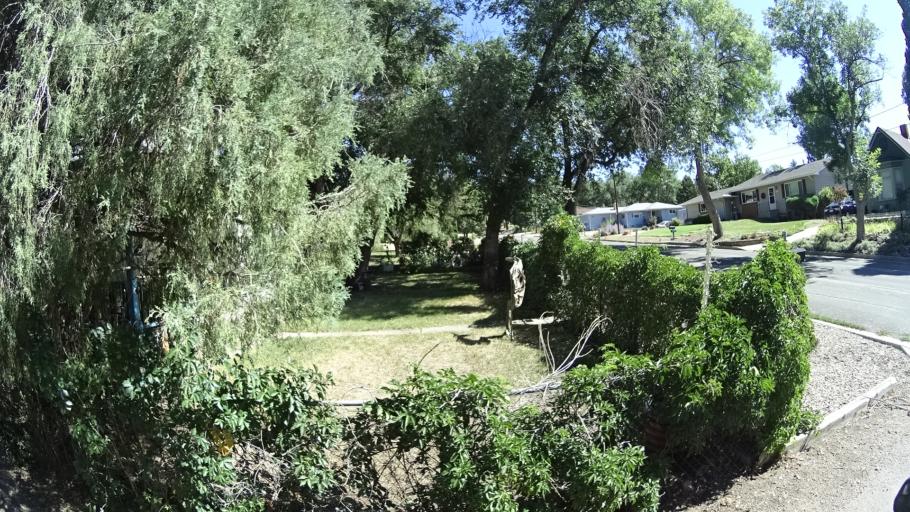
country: US
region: Colorado
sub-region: El Paso County
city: Manitou Springs
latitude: 38.8580
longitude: -104.8752
